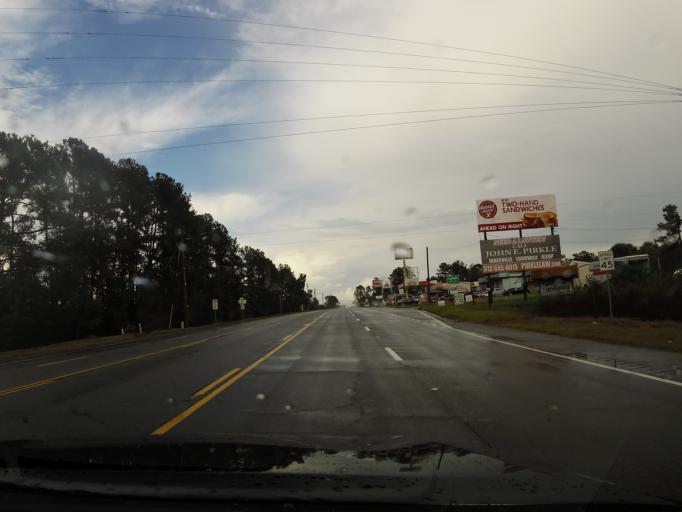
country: US
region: Georgia
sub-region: Long County
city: Ludowici
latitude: 31.7081
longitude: -81.7549
